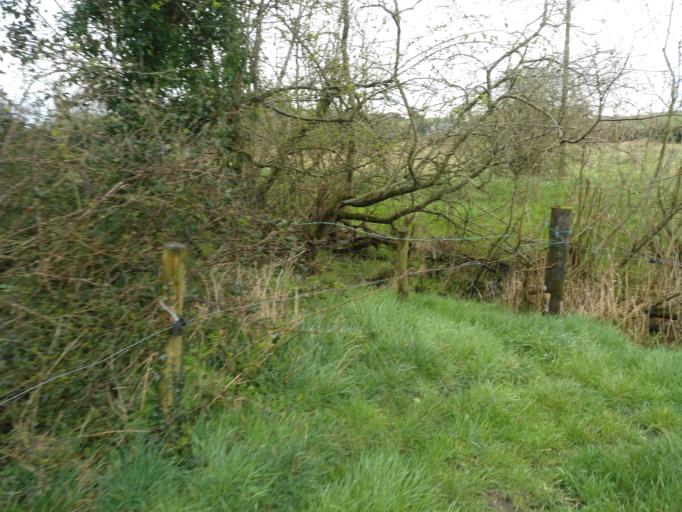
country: IE
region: Ulster
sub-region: County Monaghan
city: Clones
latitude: 54.1786
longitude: -7.2058
